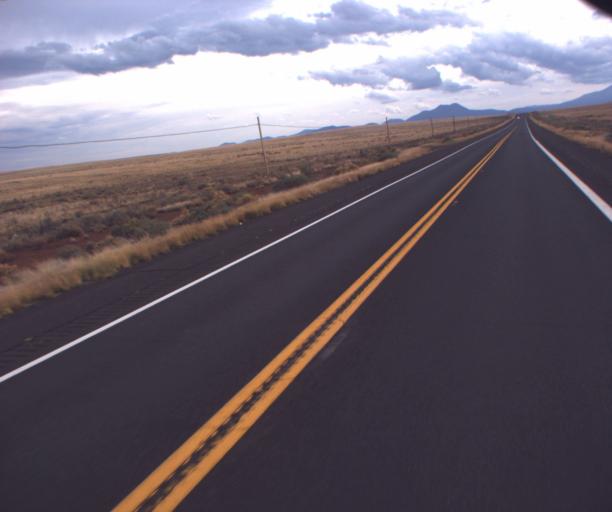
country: US
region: Arizona
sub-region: Coconino County
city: Flagstaff
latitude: 35.6445
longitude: -111.5174
